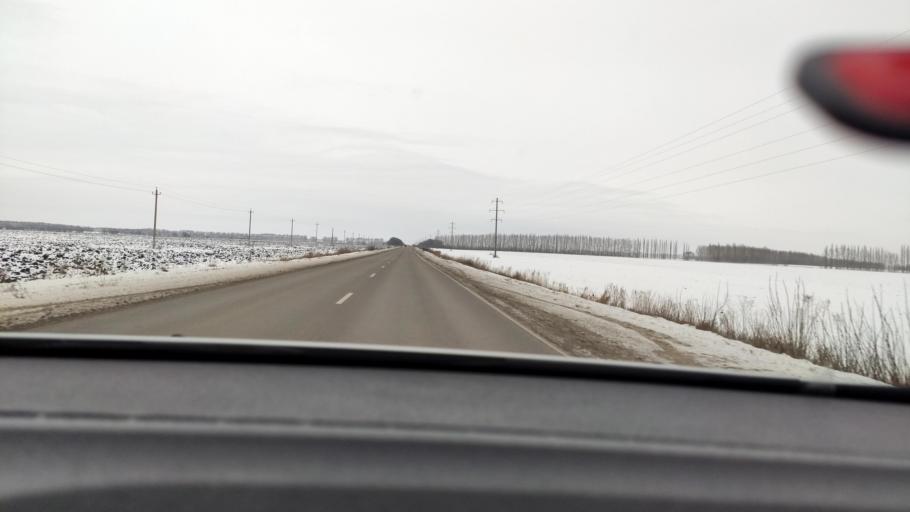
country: RU
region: Voronezj
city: Latnaya
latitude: 51.7445
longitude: 38.9366
